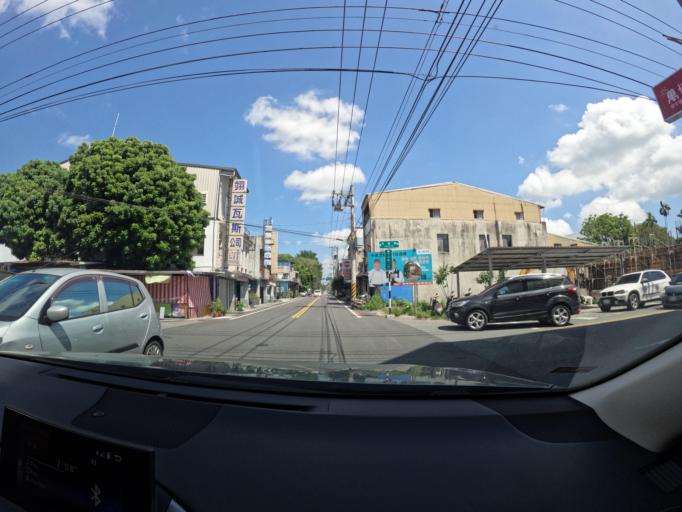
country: TW
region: Taiwan
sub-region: Hualien
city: Hualian
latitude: 23.6682
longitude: 121.4248
